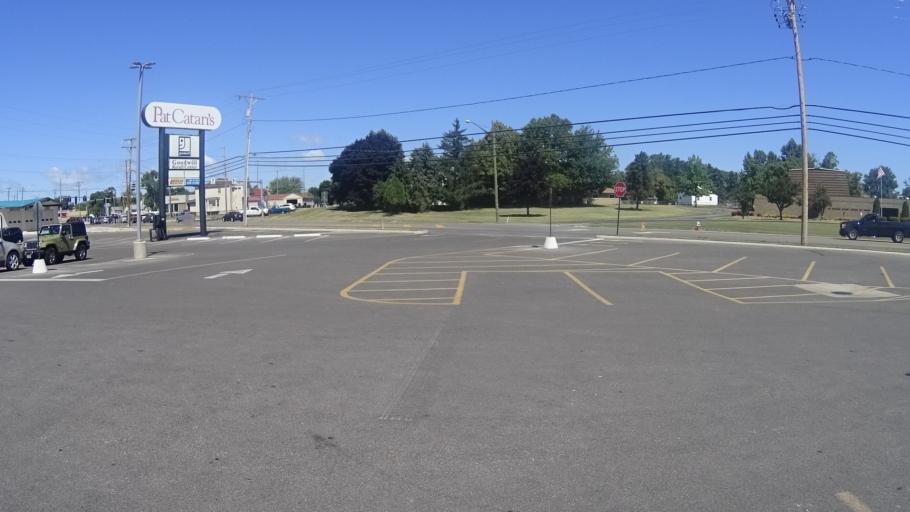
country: US
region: Ohio
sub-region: Erie County
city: Sandusky
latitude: 41.4324
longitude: -82.6864
